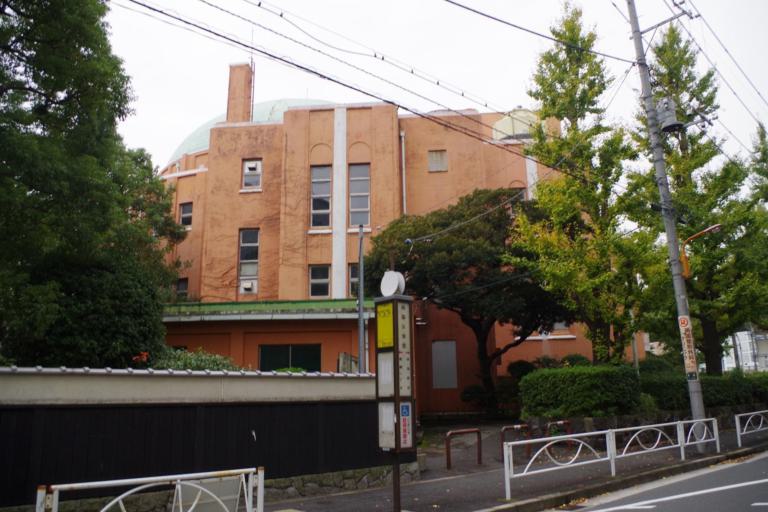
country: JP
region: Tokyo
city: Urayasu
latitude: 35.6990
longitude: 139.7941
